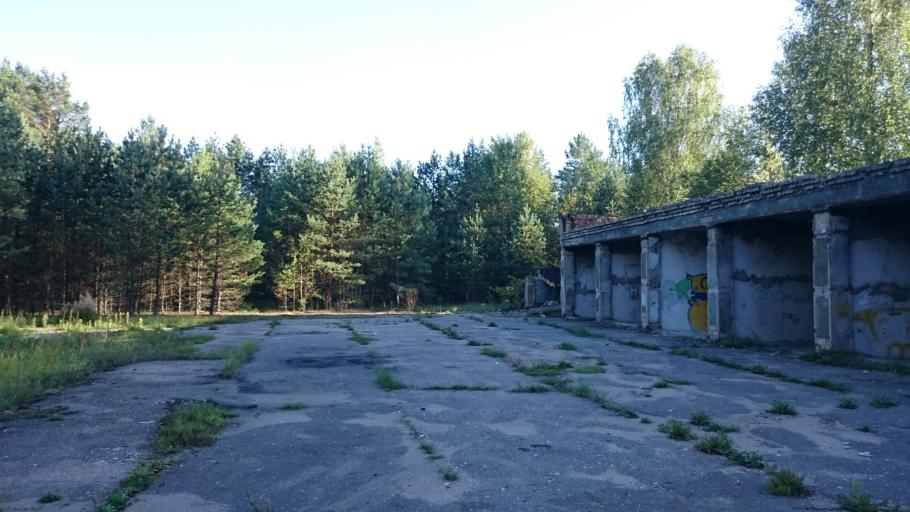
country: LV
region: Carnikava
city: Carnikava
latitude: 57.1029
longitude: 24.2350
